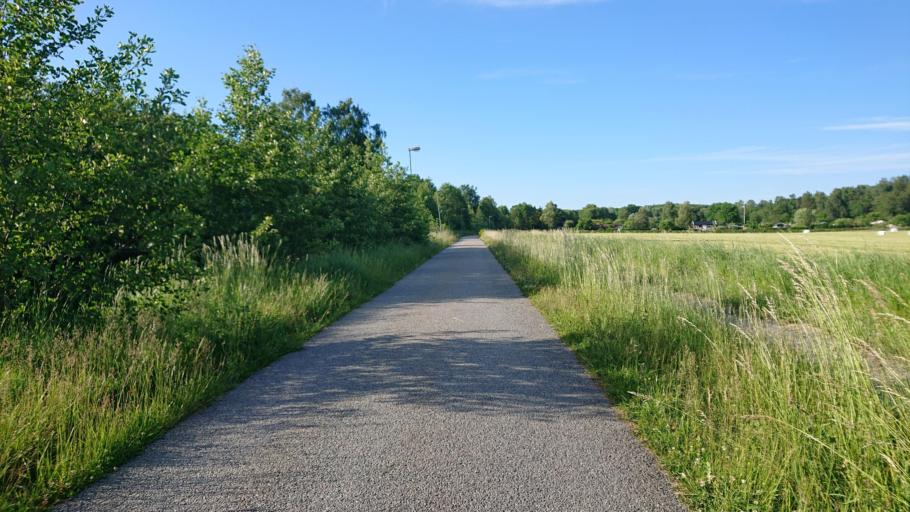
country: SE
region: Stockholm
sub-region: Osterakers Kommun
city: Akersberga
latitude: 59.4944
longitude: 18.2905
